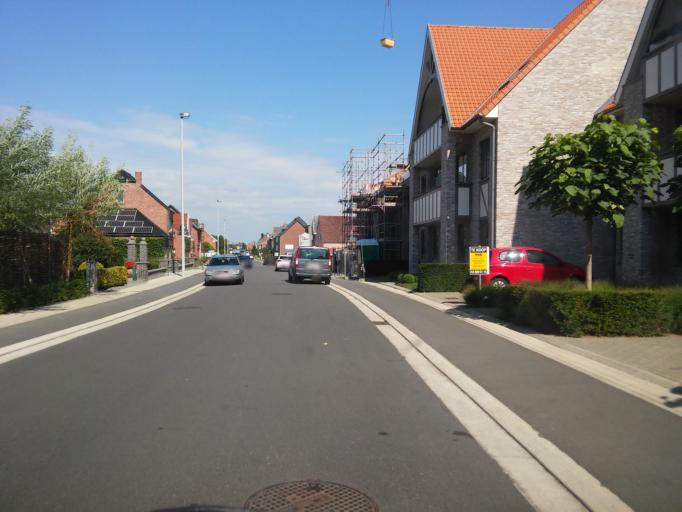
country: BE
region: Flanders
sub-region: Provincie Oost-Vlaanderen
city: Buggenhout
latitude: 51.0065
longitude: 4.2071
